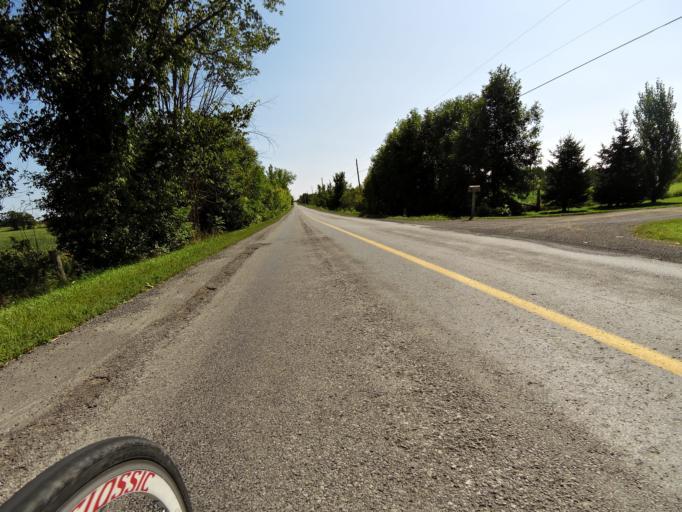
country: CA
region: Ontario
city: Bells Corners
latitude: 45.4211
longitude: -76.0443
